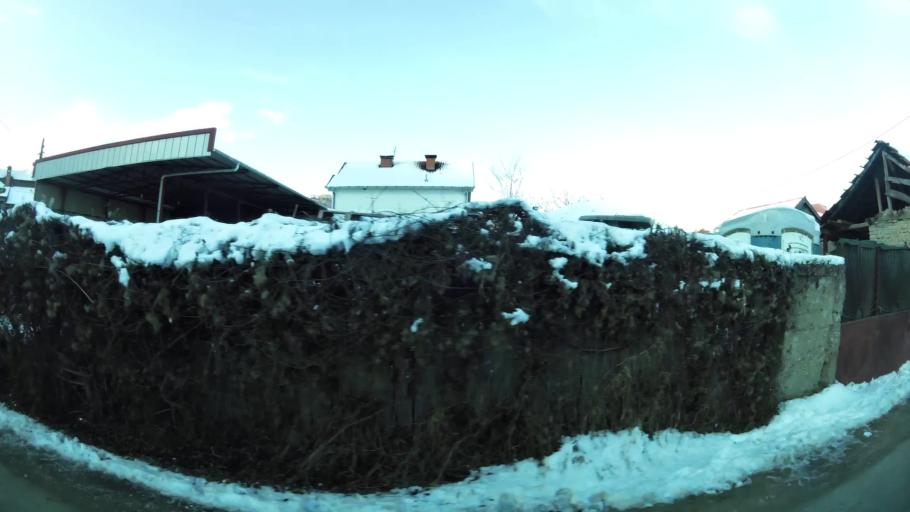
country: MK
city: Grchec
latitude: 41.9741
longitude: 21.3106
